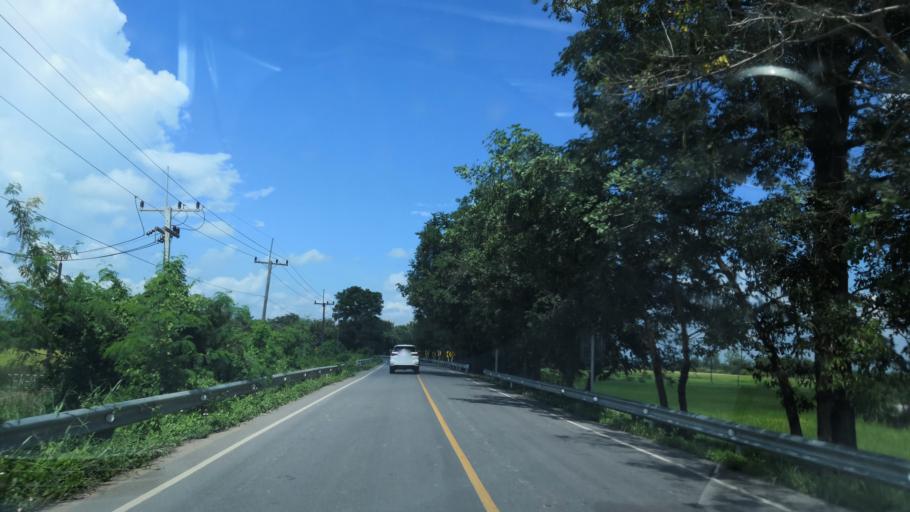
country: TH
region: Chiang Rai
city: Wiang Chiang Rung
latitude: 19.9683
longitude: 99.9810
